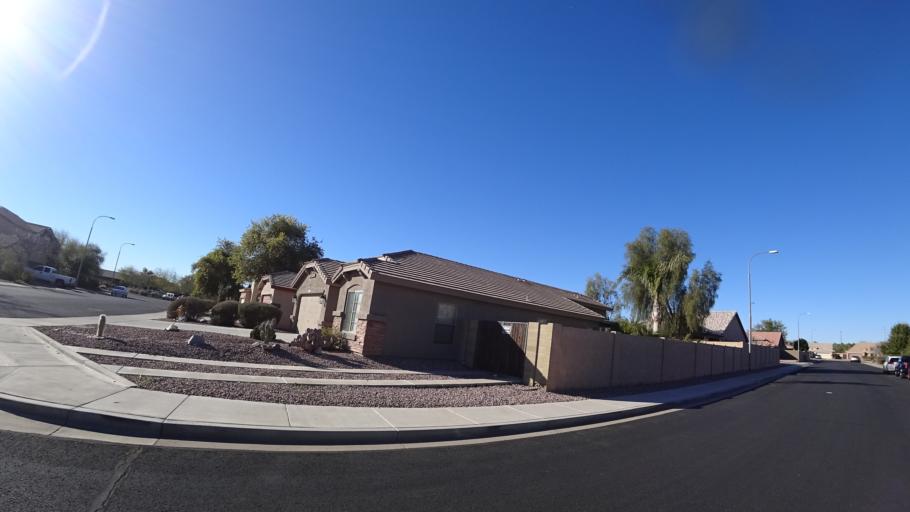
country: US
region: Arizona
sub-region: Maricopa County
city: Avondale
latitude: 33.4333
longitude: -112.3114
